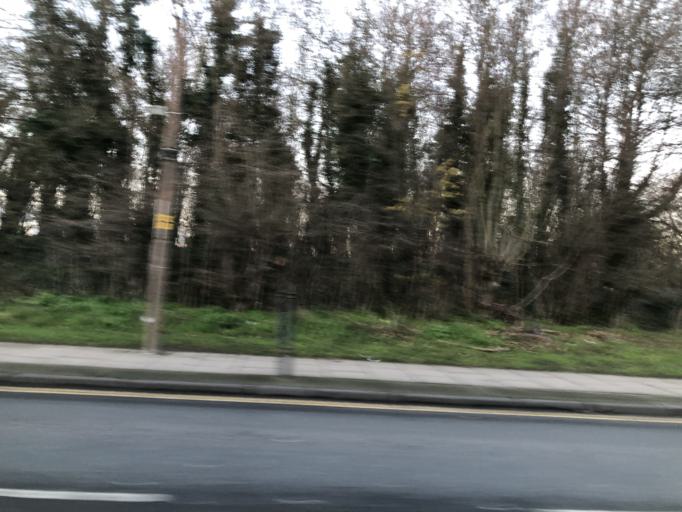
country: GB
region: England
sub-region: Greater London
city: Woolwich
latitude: 51.4719
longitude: 0.0505
